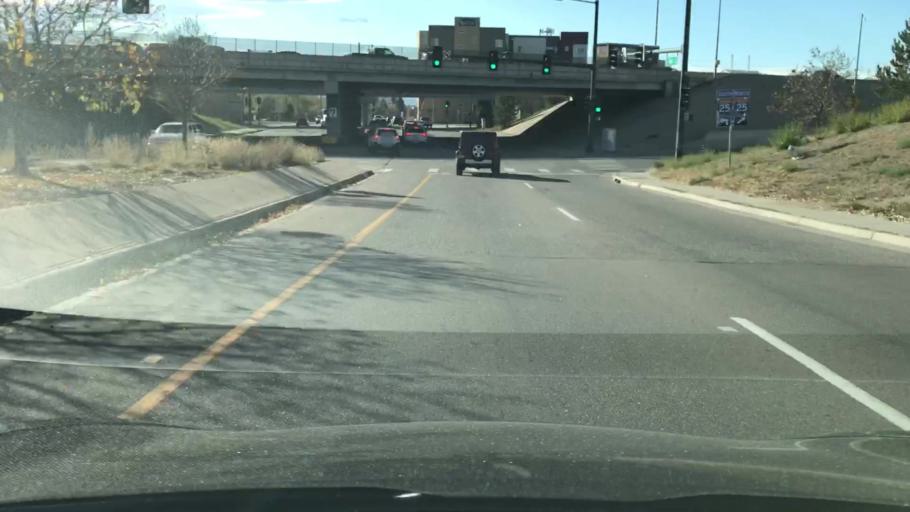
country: US
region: Colorado
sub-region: Arapahoe County
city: Glendale
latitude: 39.6676
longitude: -104.9247
